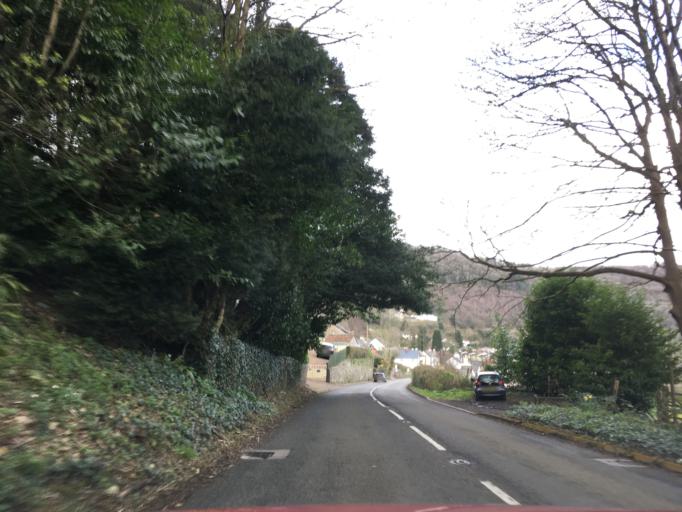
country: GB
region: Wales
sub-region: Monmouthshire
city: Tintern
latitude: 51.7301
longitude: -2.6887
